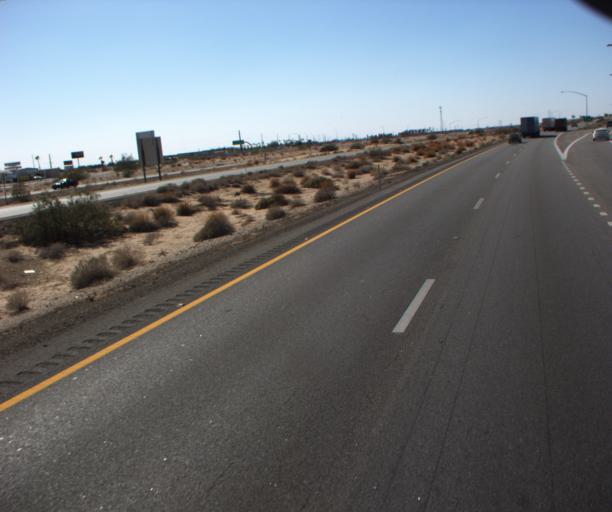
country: US
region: Arizona
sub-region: Yuma County
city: Fortuna Foothills
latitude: 32.6710
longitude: -114.4818
